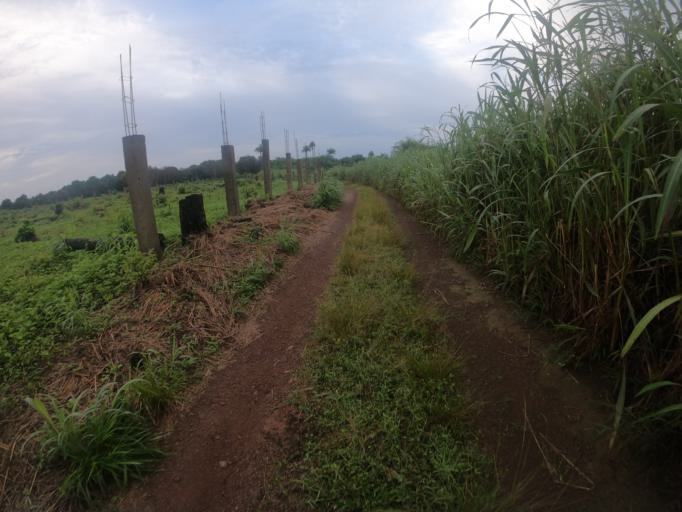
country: SL
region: Southern Province
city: Rotifunk
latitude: 8.4864
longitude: -12.7408
